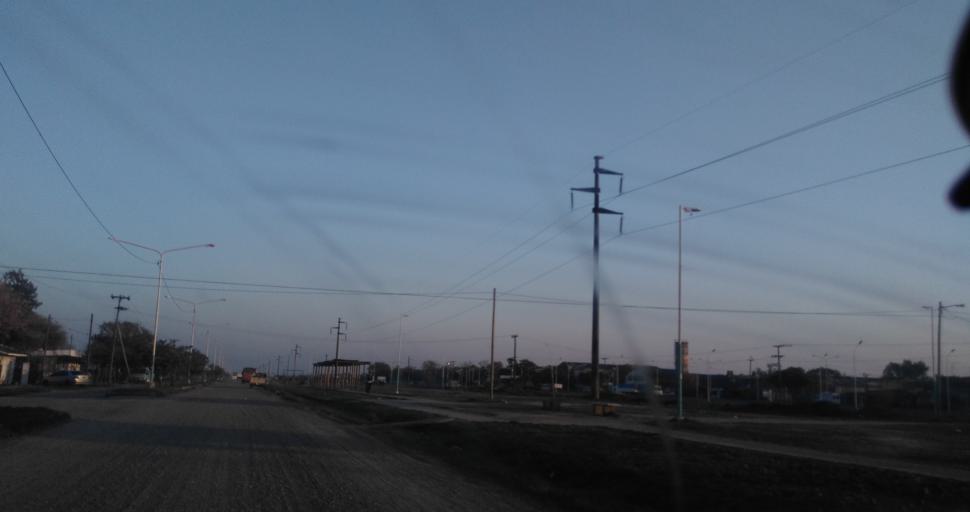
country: AR
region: Chaco
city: Resistencia
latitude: -27.4729
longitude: -59.0067
